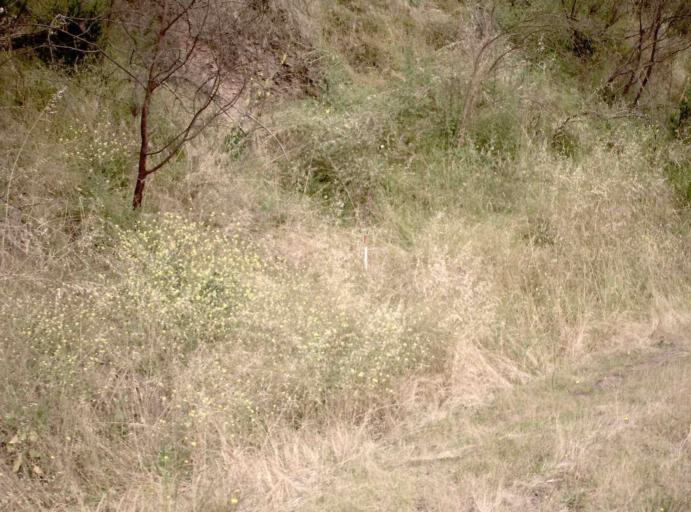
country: AU
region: Victoria
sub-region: Wellington
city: Heyfield
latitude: -37.7842
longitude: 146.6666
